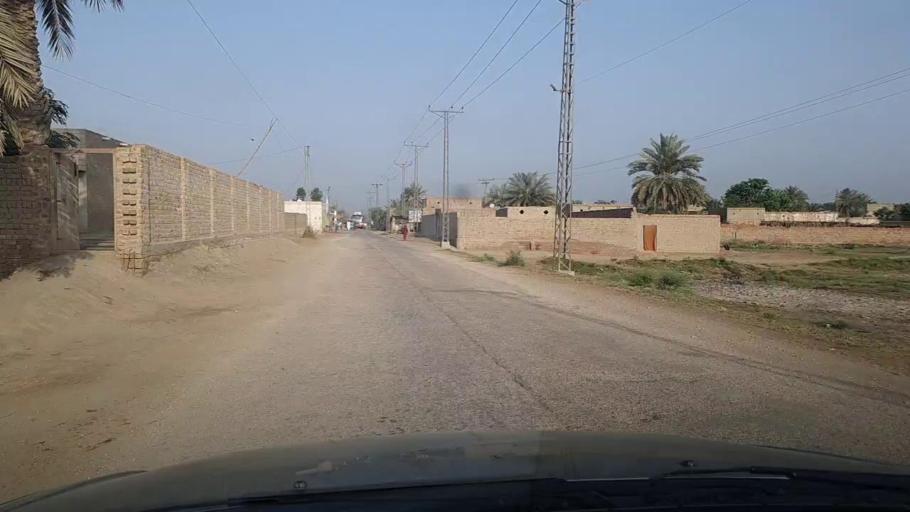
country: PK
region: Sindh
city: Pir jo Goth
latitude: 27.5702
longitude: 68.6294
